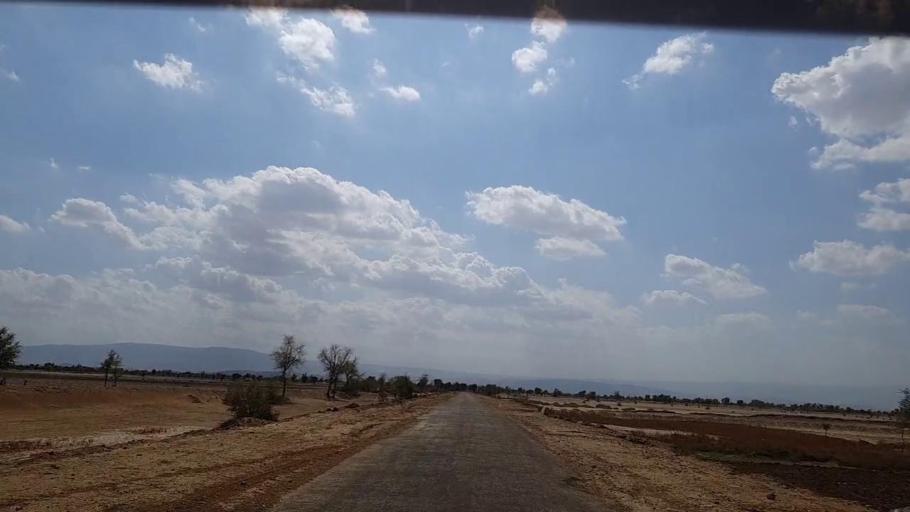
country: PK
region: Sindh
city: Johi
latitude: 26.5221
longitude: 67.4964
